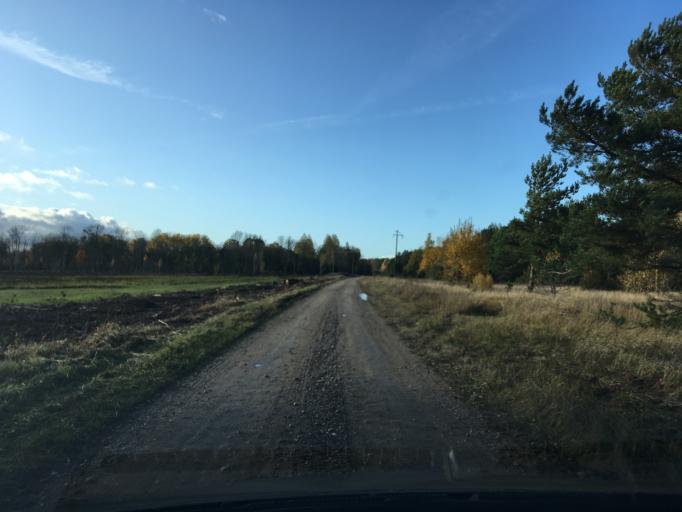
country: EE
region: Laeaene
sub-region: Lihula vald
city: Lihula
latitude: 58.5646
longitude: 23.7717
